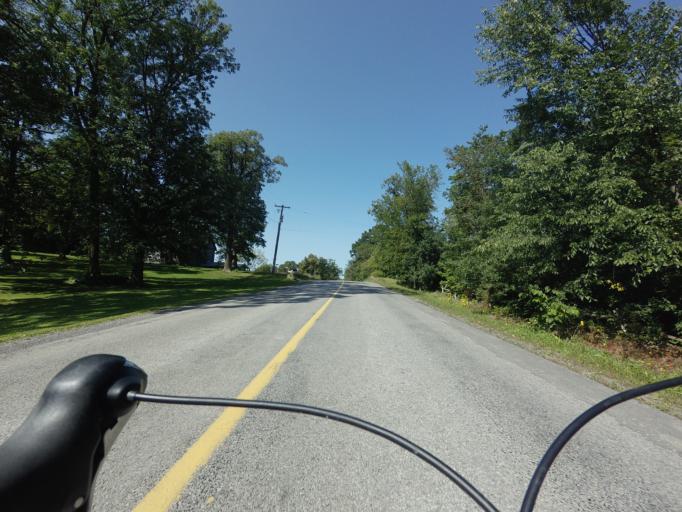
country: CA
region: Ontario
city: Bells Corners
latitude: 45.4219
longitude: -76.0453
